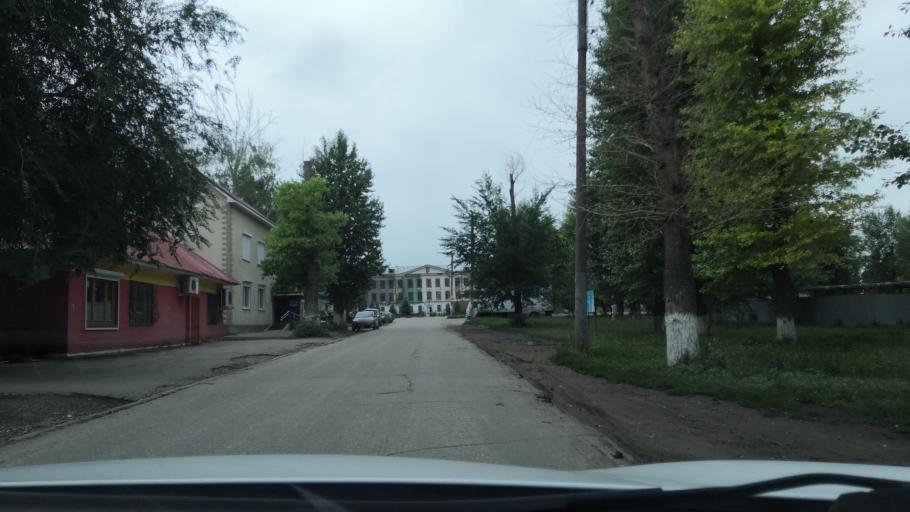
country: RU
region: Samara
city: Smyshlyayevka
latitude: 53.2692
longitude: 50.3947
